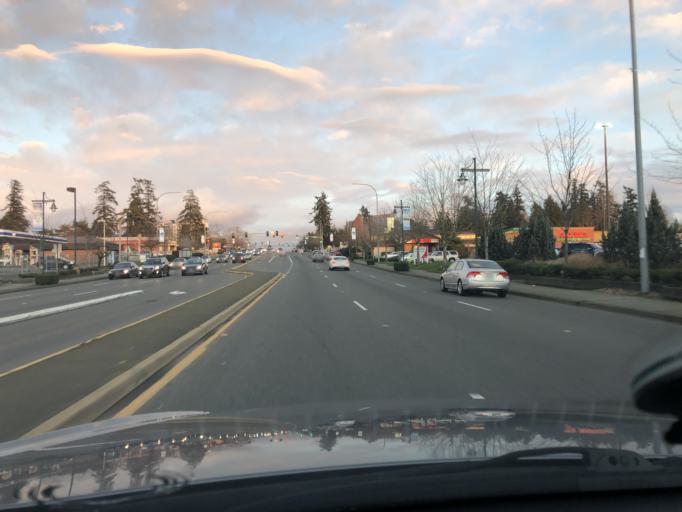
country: US
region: Washington
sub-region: King County
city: Federal Way
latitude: 47.3150
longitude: -122.3059
